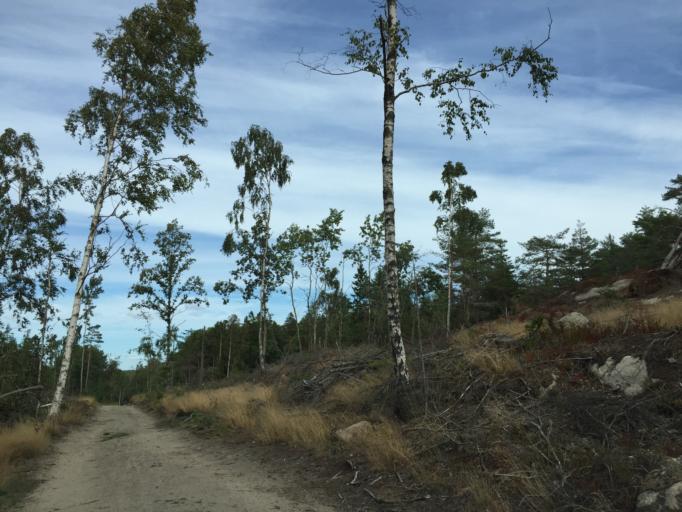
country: NO
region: Ostfold
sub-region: Fredrikstad
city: Fredrikstad
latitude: 59.0964
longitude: 10.9265
